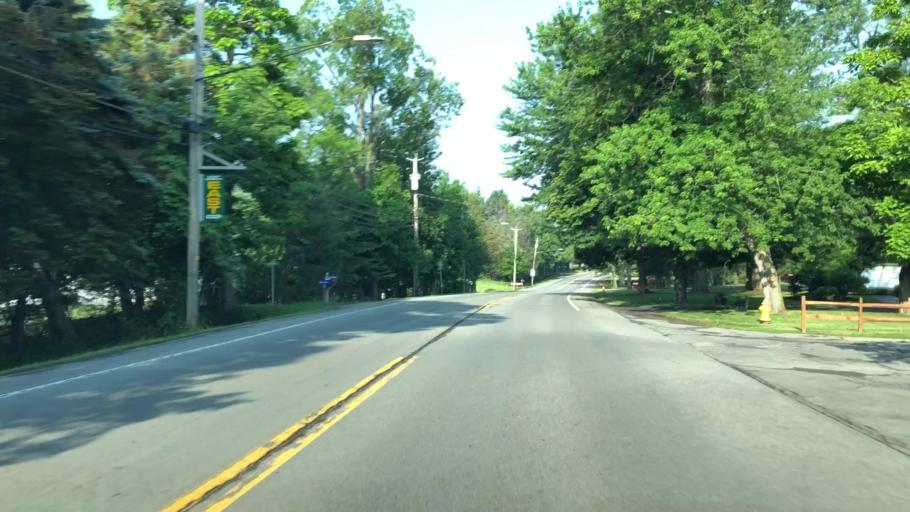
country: US
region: New York
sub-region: Erie County
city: Orchard Park
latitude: 42.8310
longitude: -78.7274
